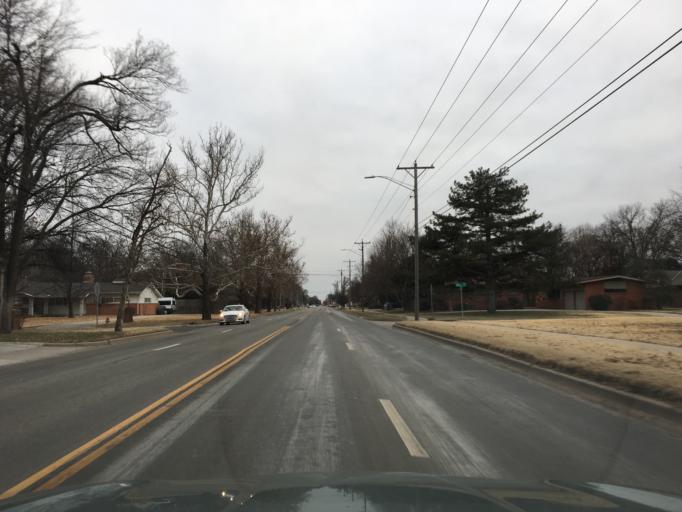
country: US
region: Kansas
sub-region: Sedgwick County
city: Bellaire
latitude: 37.6999
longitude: -97.2622
